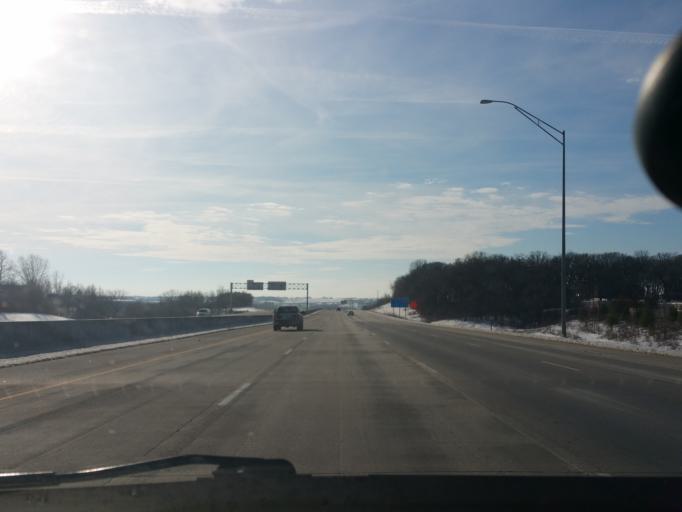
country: US
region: Iowa
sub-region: Polk County
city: West Des Moines
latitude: 41.5523
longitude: -93.7765
